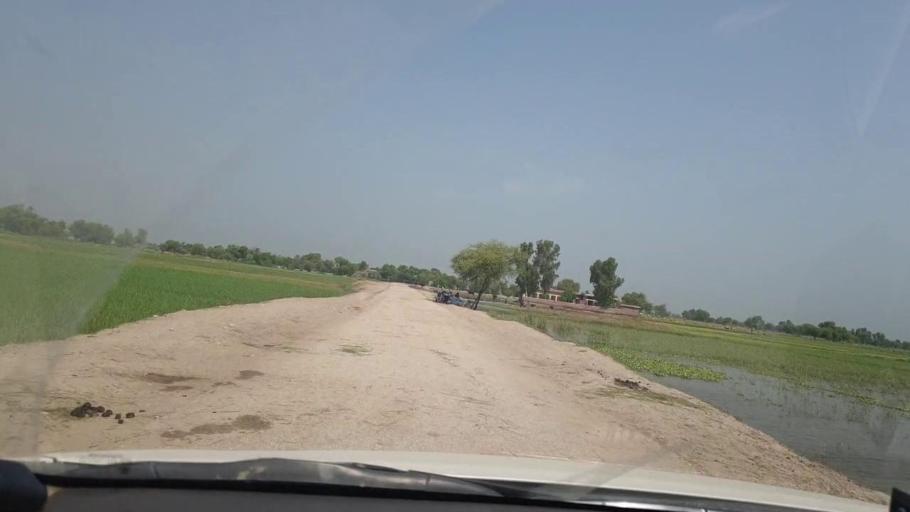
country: PK
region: Sindh
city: Chak
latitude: 27.8769
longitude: 68.7836
